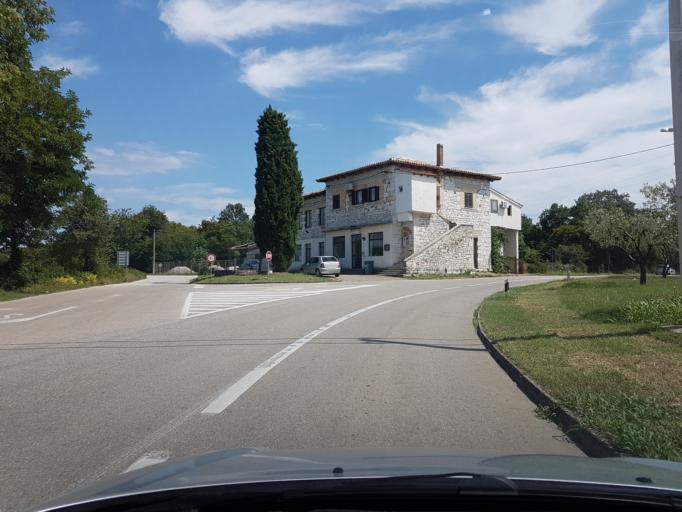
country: HR
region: Istarska
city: Vrsar
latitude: 45.1596
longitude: 13.6906
